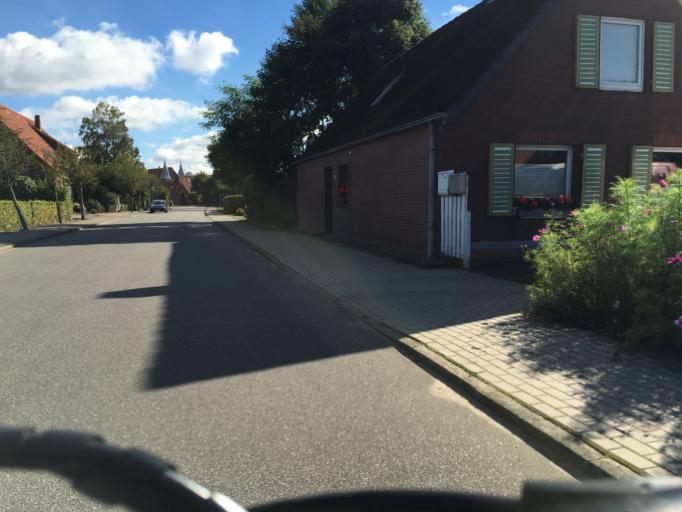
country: DE
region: Lower Saxony
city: Bardowick
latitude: 53.3018
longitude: 10.3819
